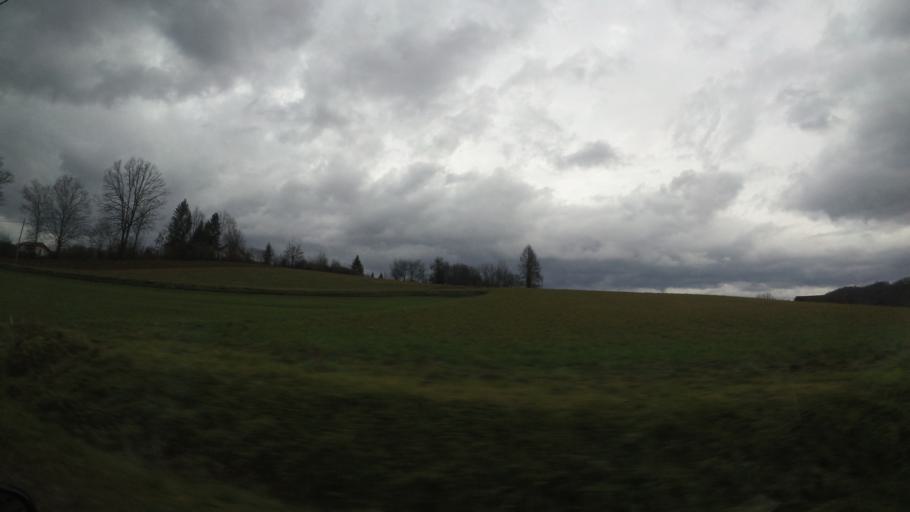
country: HR
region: Karlovacka
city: Vojnic
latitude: 45.3213
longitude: 15.6767
